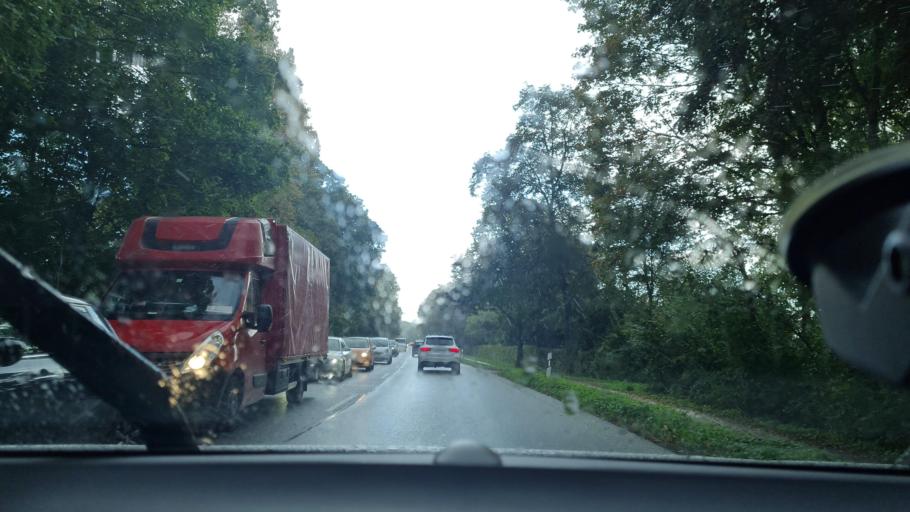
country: DE
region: North Rhine-Westphalia
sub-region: Regierungsbezirk Dusseldorf
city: Dinslaken
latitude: 51.5627
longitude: 6.7250
